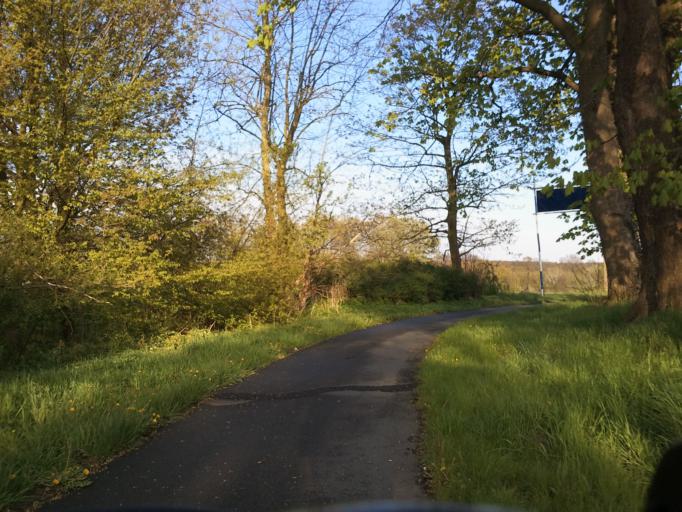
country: DE
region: Lower Saxony
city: Heemsen
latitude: 52.6645
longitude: 9.2543
